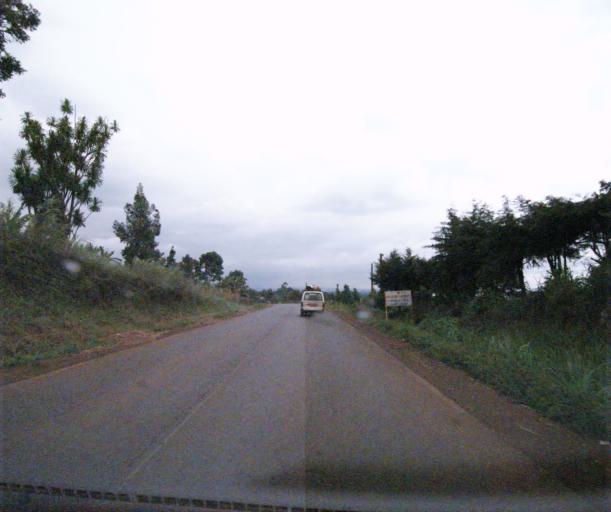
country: CM
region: West
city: Bansoa
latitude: 5.4898
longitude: 10.1933
